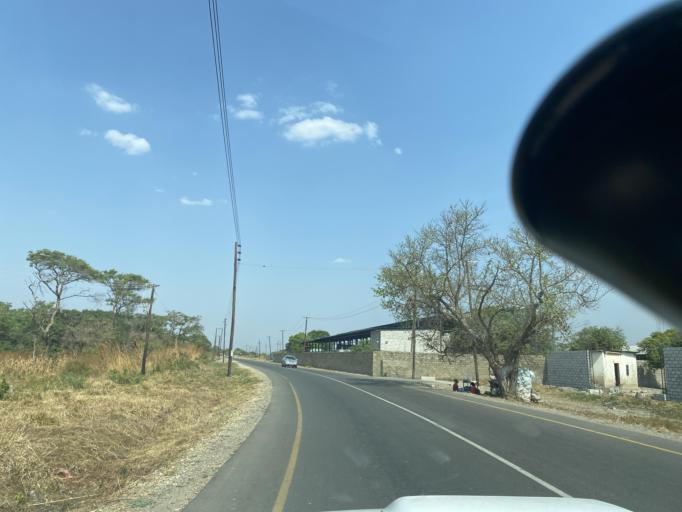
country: ZM
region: Lusaka
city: Lusaka
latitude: -15.3407
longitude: 28.0774
